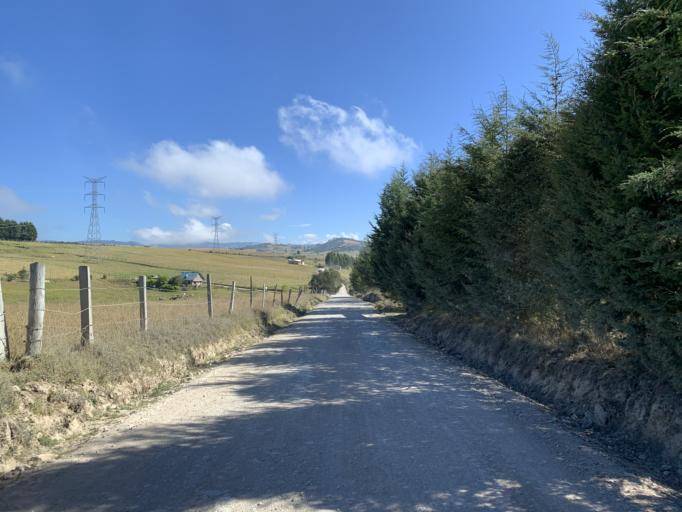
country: CO
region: Boyaca
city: Tuta
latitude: 5.6671
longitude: -73.1501
